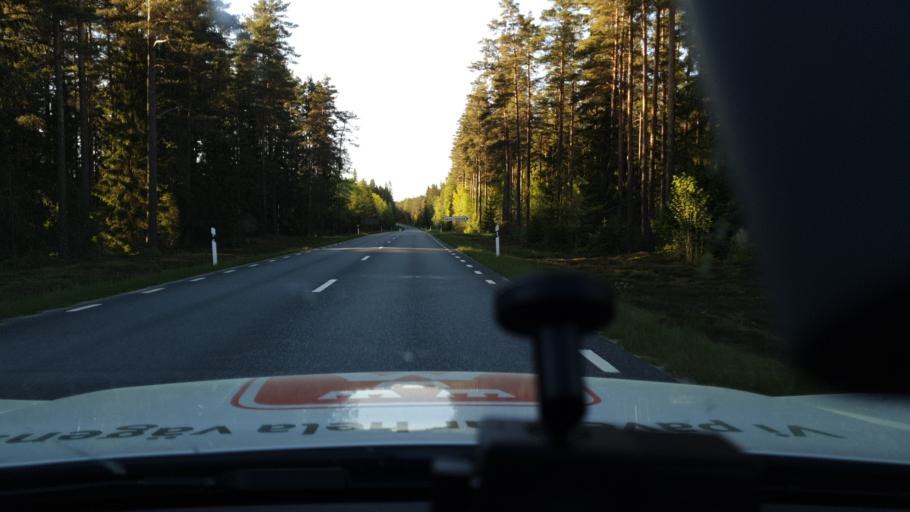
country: SE
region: Joenkoeping
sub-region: Vetlanda Kommun
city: Ekenassjon
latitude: 57.5754
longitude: 14.9721
